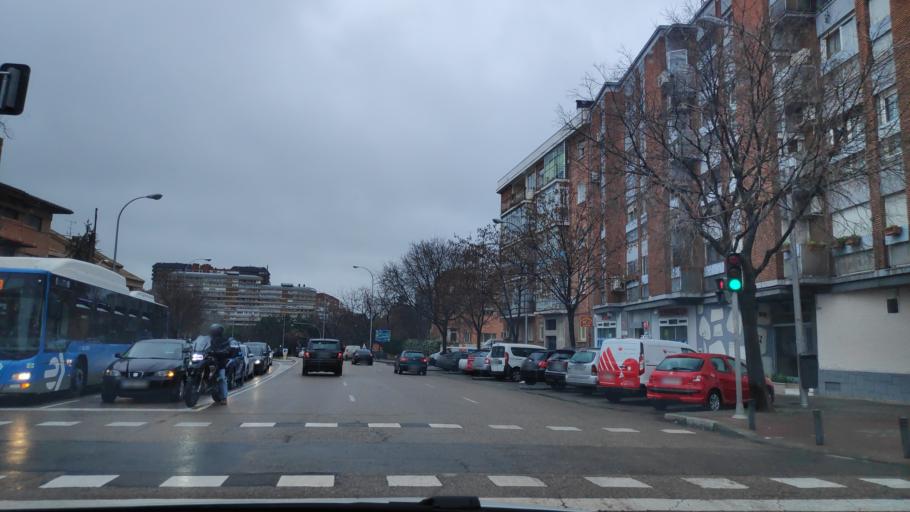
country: ES
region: Madrid
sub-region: Provincia de Madrid
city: Chamartin
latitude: 40.4523
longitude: -3.6674
